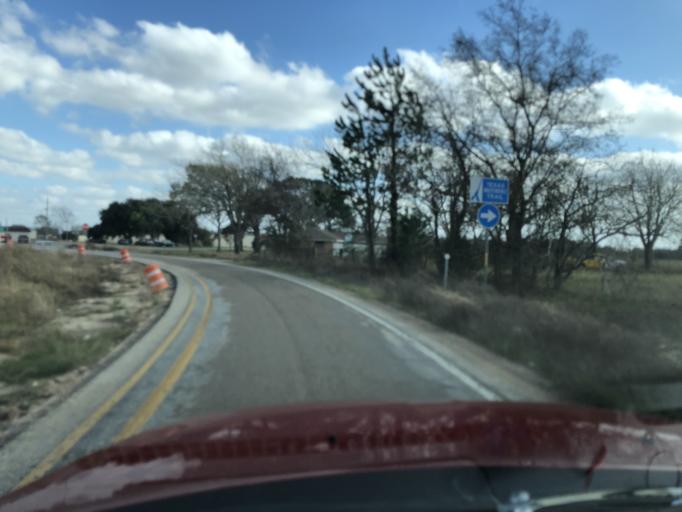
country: US
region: Texas
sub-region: Austin County
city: Sealy
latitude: 29.7744
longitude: -96.1094
